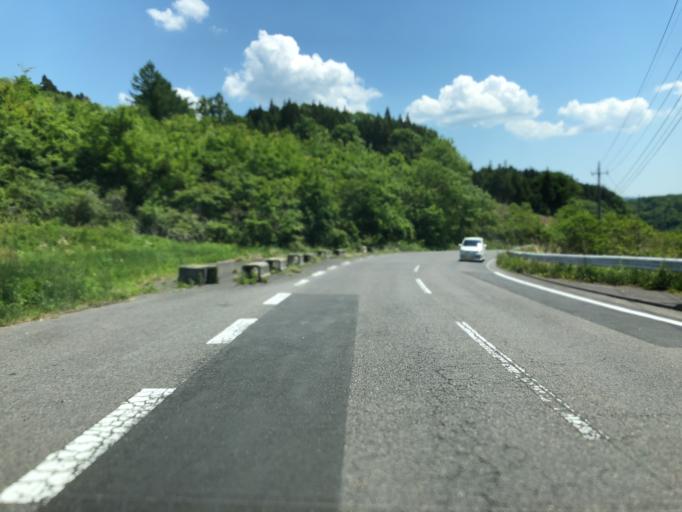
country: JP
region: Fukushima
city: Funehikimachi-funehiki
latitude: 37.4831
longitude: 140.5621
